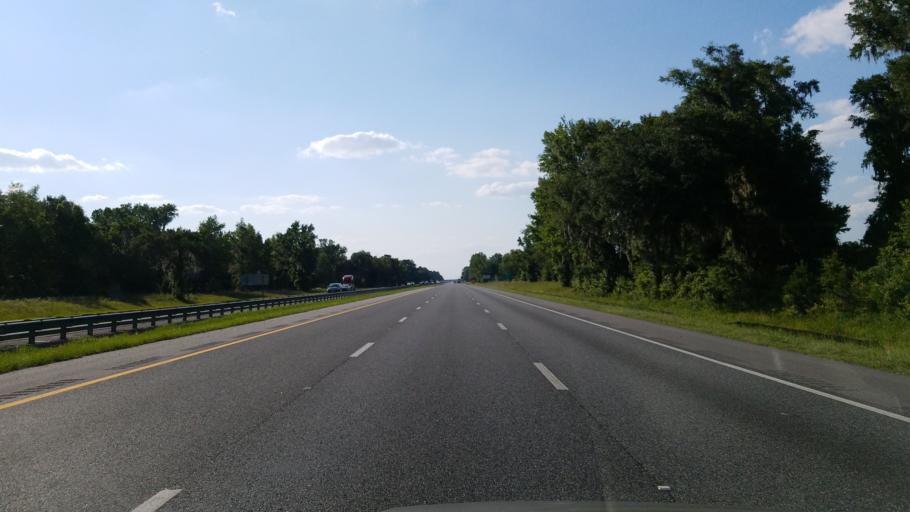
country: US
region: Florida
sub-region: Hamilton County
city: Jasper
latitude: 30.3958
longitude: -82.8808
